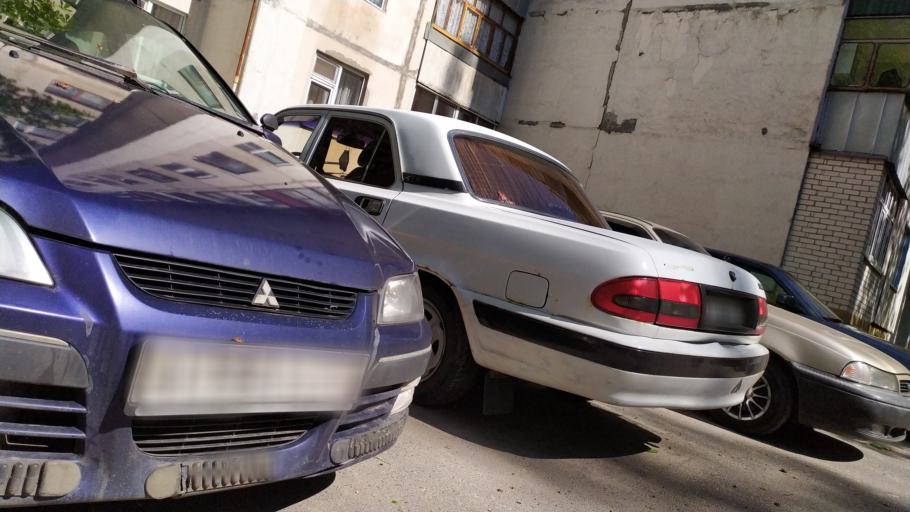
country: RU
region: Kursk
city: Kursk
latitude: 51.7449
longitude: 36.1352
